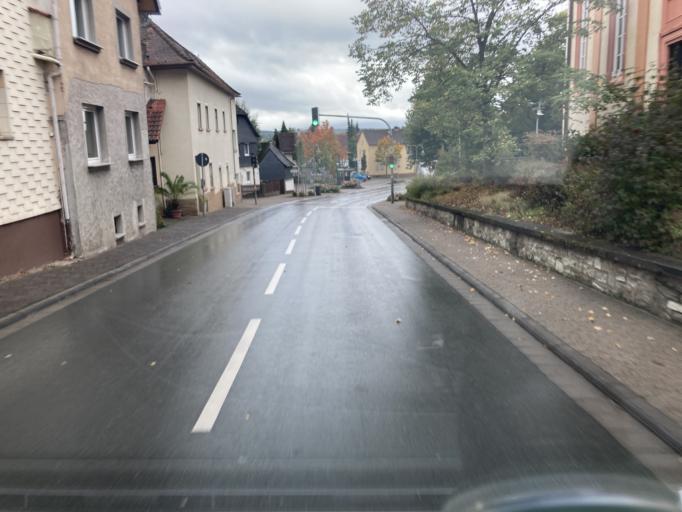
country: DE
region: Hesse
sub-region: Regierungsbezirk Darmstadt
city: Usingen
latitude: 50.3556
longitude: 8.5368
